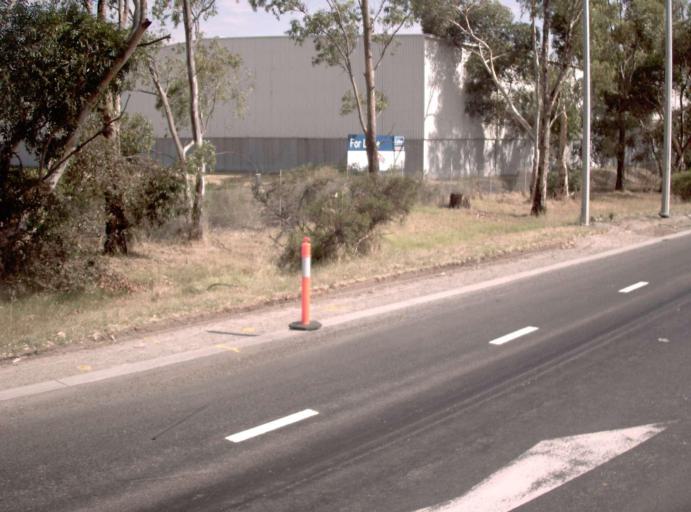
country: AU
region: Victoria
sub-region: Casey
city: Hampton Park
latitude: -38.0215
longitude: 145.2478
